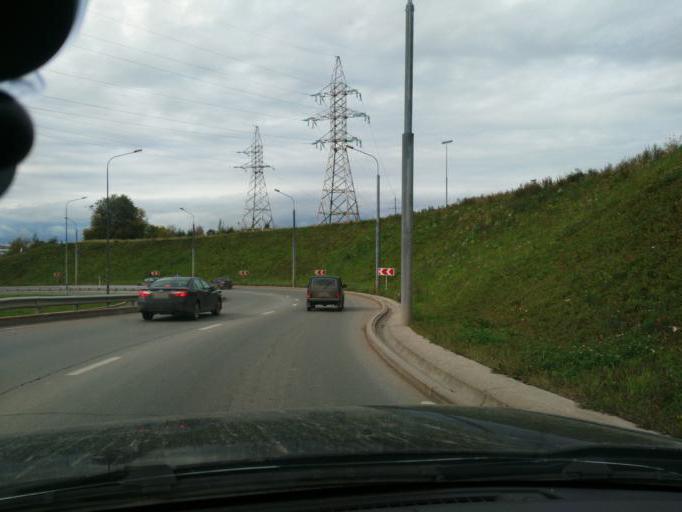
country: RU
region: Perm
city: Perm
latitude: 58.0050
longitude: 56.3195
